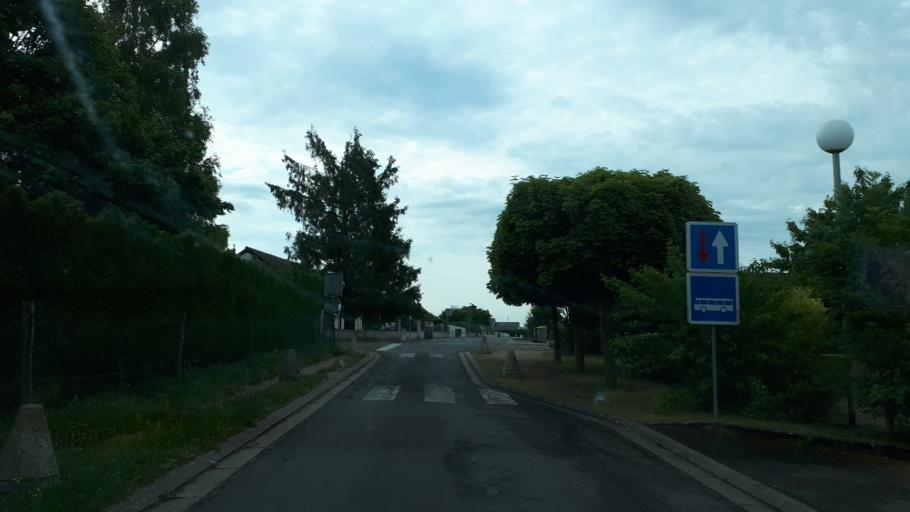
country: FR
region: Centre
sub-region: Departement du Loir-et-Cher
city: Naveil
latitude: 47.7706
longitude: 1.0105
